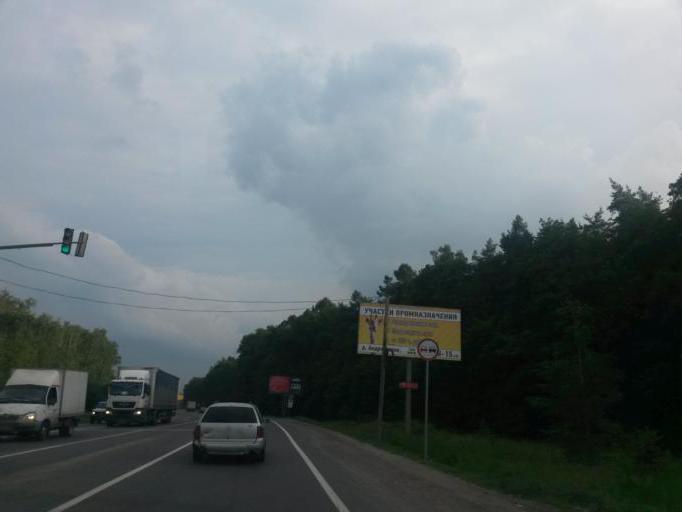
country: RU
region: Moskovskaya
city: Petrovskaya
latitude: 55.5323
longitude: 37.7678
